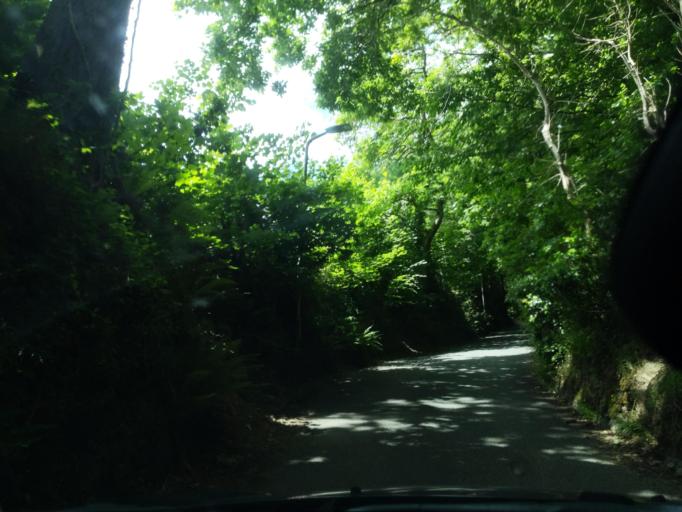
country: GB
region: England
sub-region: Devon
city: Plympton
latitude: 50.4132
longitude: -4.0823
